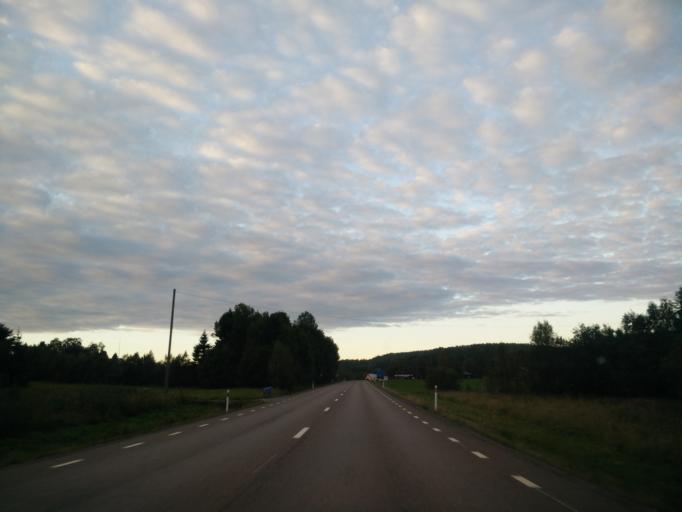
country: SE
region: Vaesternorrland
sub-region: Kramfors Kommun
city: Nordingra
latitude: 62.9277
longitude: 18.0830
